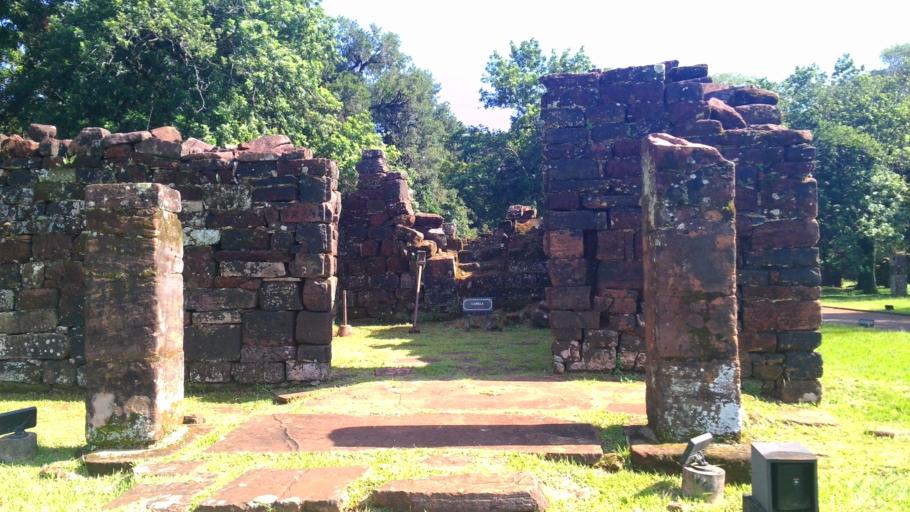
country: AR
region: Misiones
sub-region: Departamento de San Ignacio
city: San Ignacio
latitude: -27.2537
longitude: -55.5316
